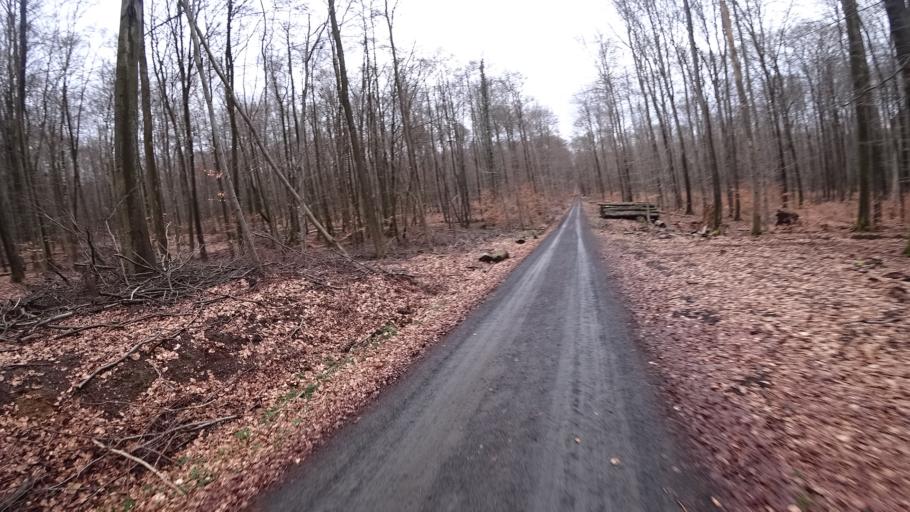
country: DE
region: Rheinland-Pfalz
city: Dernbach
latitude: 50.4319
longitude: 7.7851
